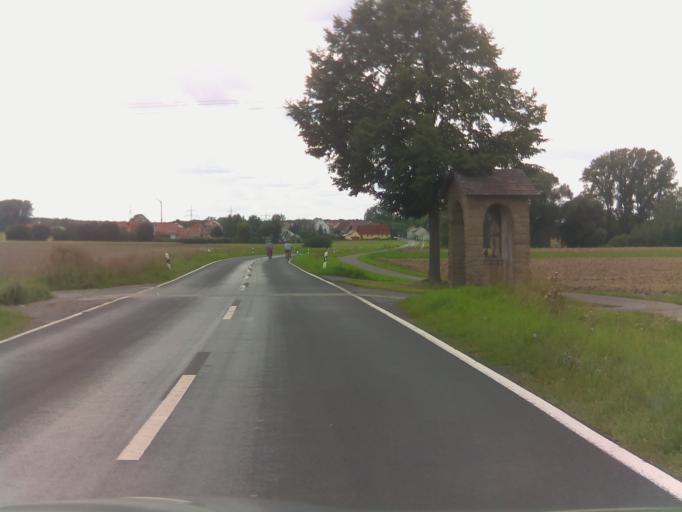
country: DE
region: Bavaria
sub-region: Regierungsbezirk Unterfranken
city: Donnersdorf
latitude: 49.9828
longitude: 10.3785
